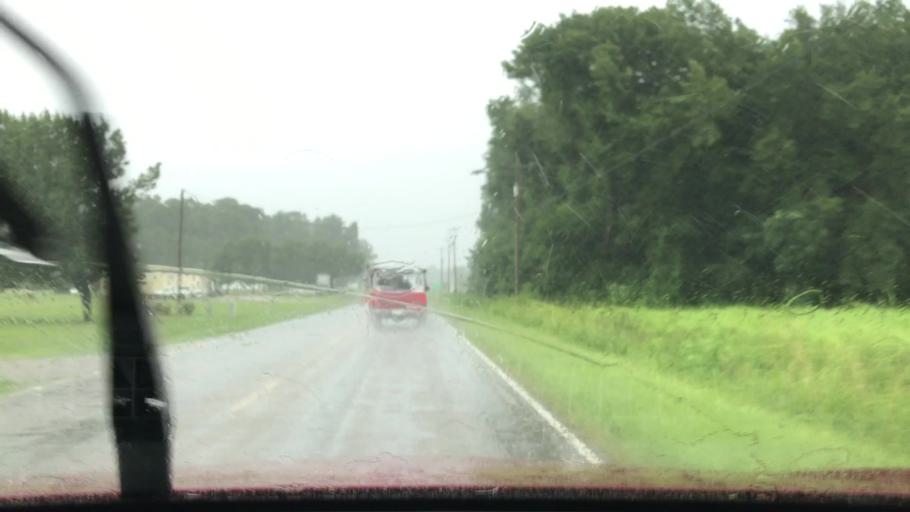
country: US
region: South Carolina
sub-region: Horry County
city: Red Hill
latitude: 33.8615
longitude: -78.9943
